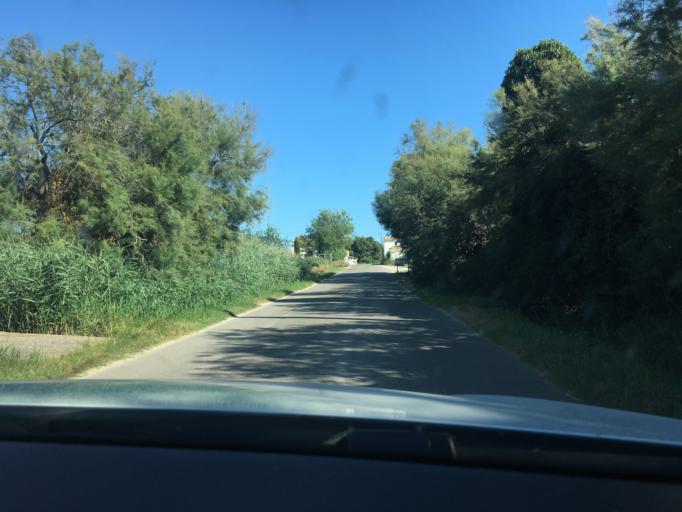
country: FR
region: Provence-Alpes-Cote d'Azur
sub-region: Departement des Bouches-du-Rhone
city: Saintes-Maries-de-la-Mer
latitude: 43.5455
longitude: 4.3461
